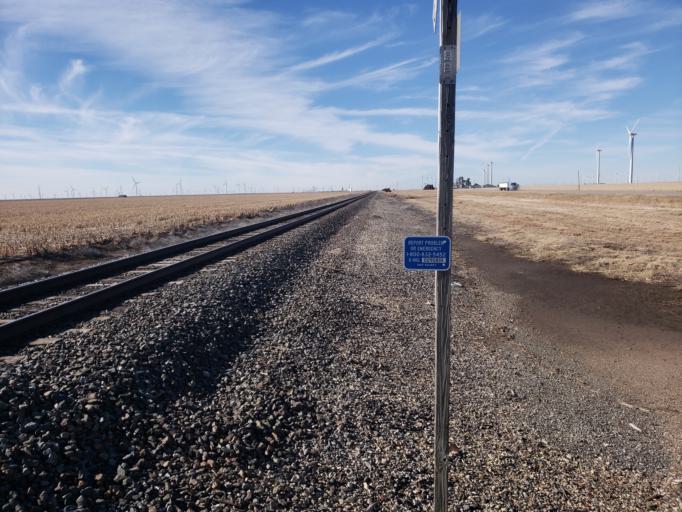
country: US
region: Kansas
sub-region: Hodgeman County
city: Jetmore
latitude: 37.8652
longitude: -99.6983
